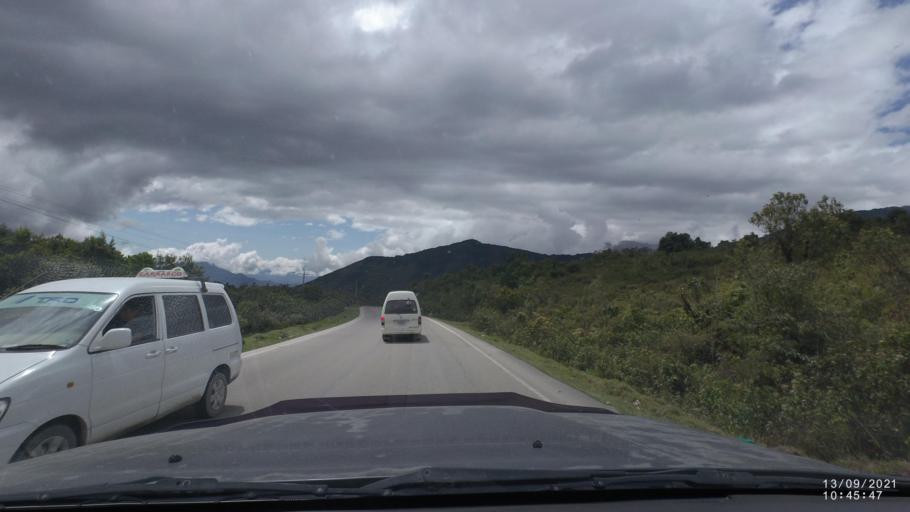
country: BO
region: Cochabamba
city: Colomi
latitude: -17.2037
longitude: -65.8727
